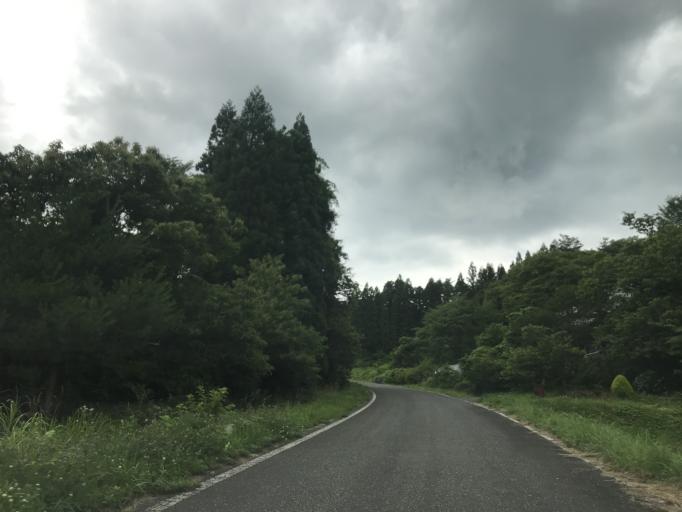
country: JP
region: Iwate
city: Ichinoseki
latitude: 38.9547
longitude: 141.0456
